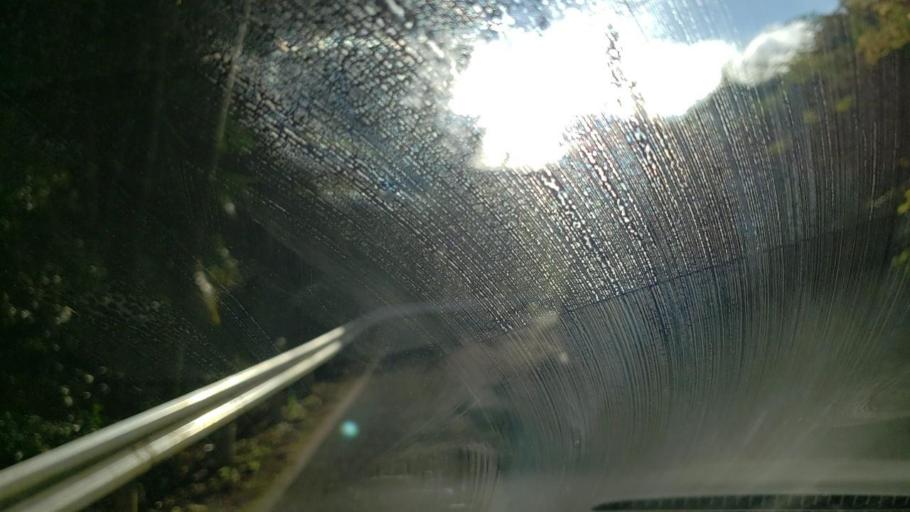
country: JP
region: Tokushima
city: Wakimachi
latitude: 34.0974
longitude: 134.0671
